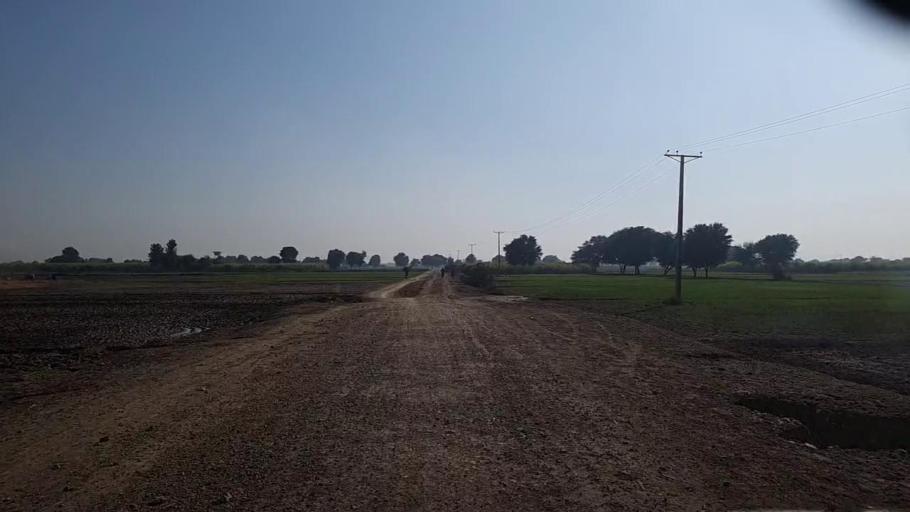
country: PK
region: Sindh
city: Darya Khan Marri
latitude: 26.6610
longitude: 68.3363
